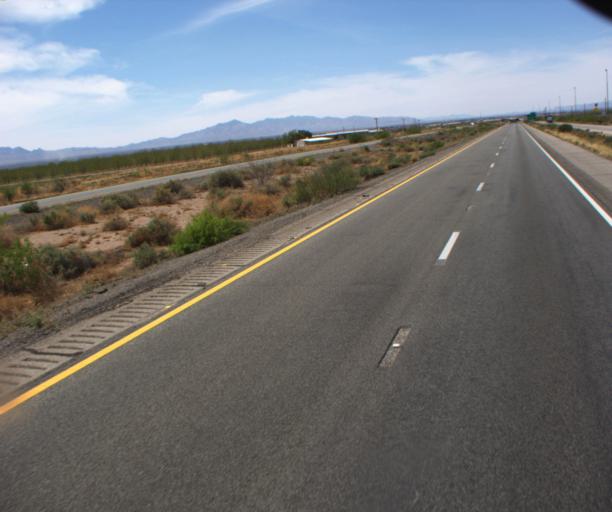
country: US
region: New Mexico
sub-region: Hidalgo County
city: Lordsburg
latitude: 32.2557
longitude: -109.1701
